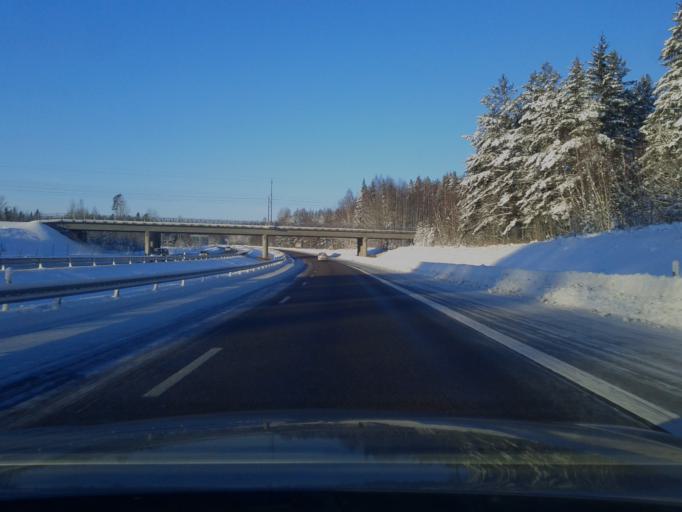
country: SE
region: Uppsala
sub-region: Alvkarleby Kommun
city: AElvkarleby
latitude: 60.4660
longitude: 17.4096
